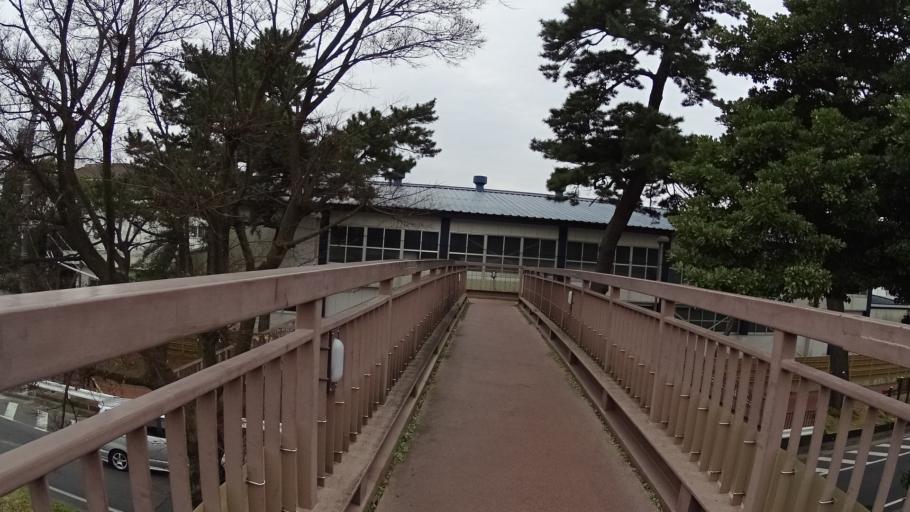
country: JP
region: Kanagawa
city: Oiso
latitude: 35.3081
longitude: 139.3080
